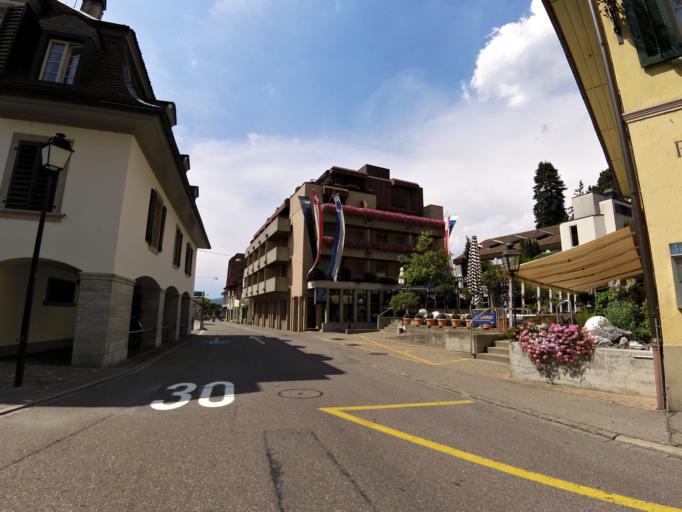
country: CH
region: Aargau
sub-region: Bezirk Lenzburg
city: Lenzburg
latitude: 47.3878
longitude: 8.1815
